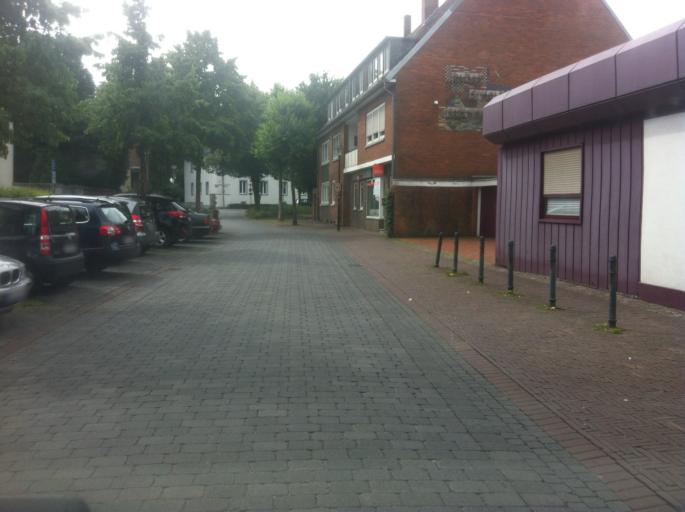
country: DE
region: North Rhine-Westphalia
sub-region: Regierungsbezirk Dusseldorf
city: Emmerich
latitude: 51.8330
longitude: 6.2479
